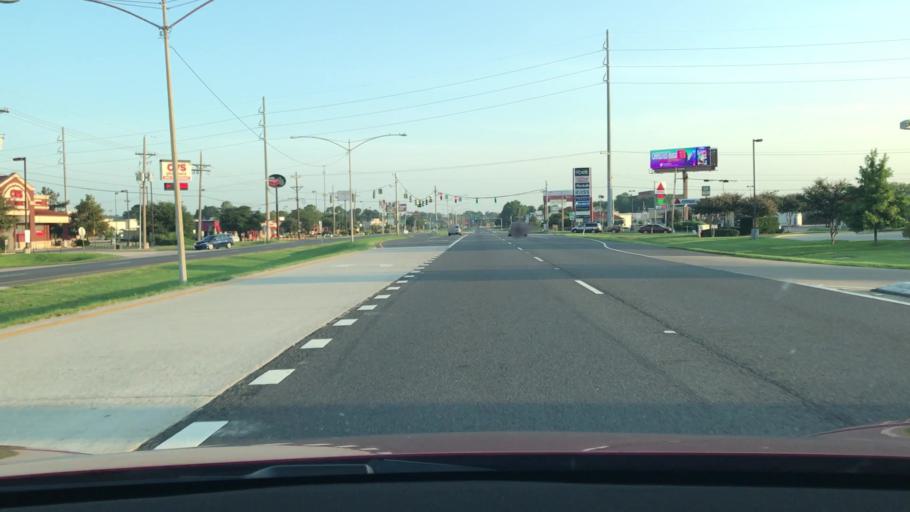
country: US
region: Louisiana
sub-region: Bossier Parish
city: Bossier City
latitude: 32.4423
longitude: -93.7178
